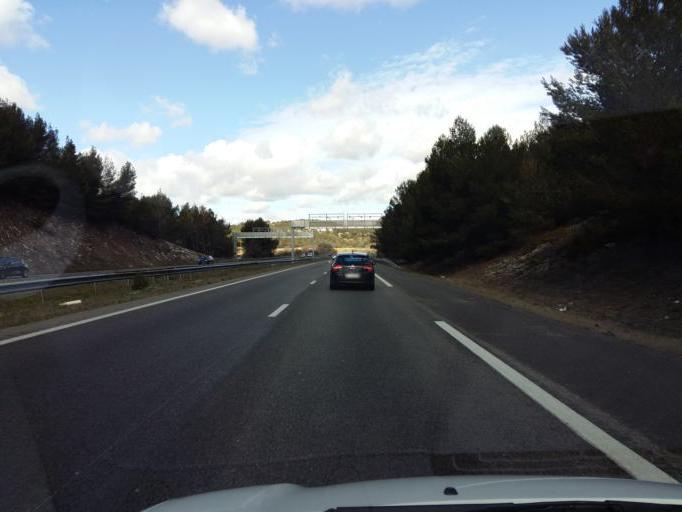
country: FR
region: Provence-Alpes-Cote d'Azur
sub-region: Departement des Bouches-du-Rhone
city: Cabries
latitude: 43.4454
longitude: 5.3961
